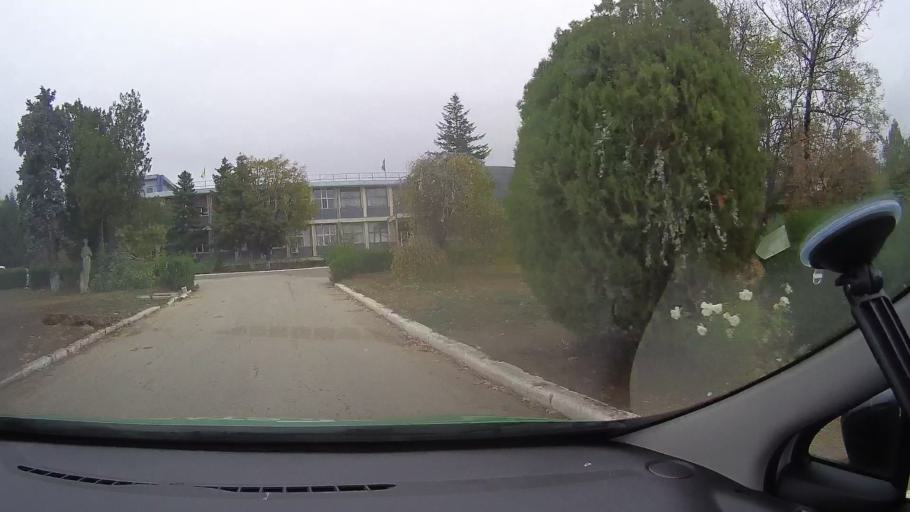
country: RO
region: Constanta
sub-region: Oras Murfatlar
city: Murfatlar
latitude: 44.1767
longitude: 28.4229
